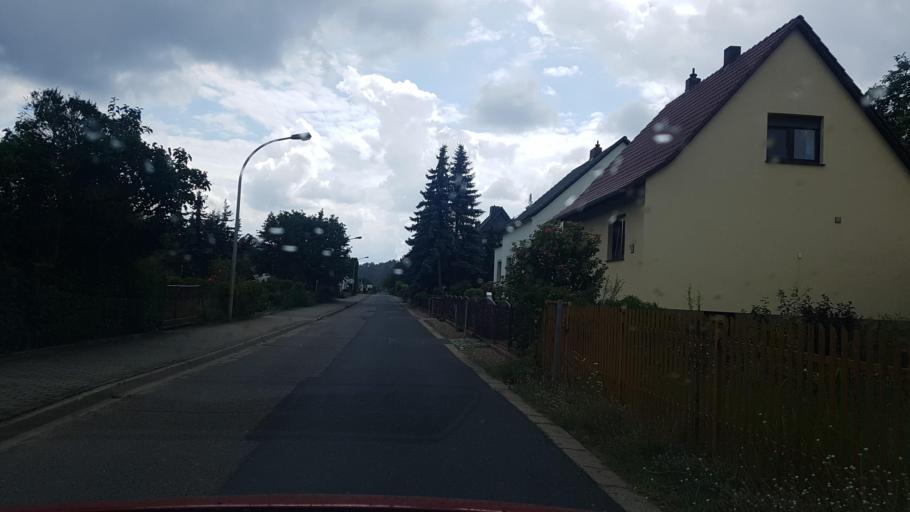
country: DE
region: Brandenburg
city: Herzberg
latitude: 51.6870
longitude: 13.2427
